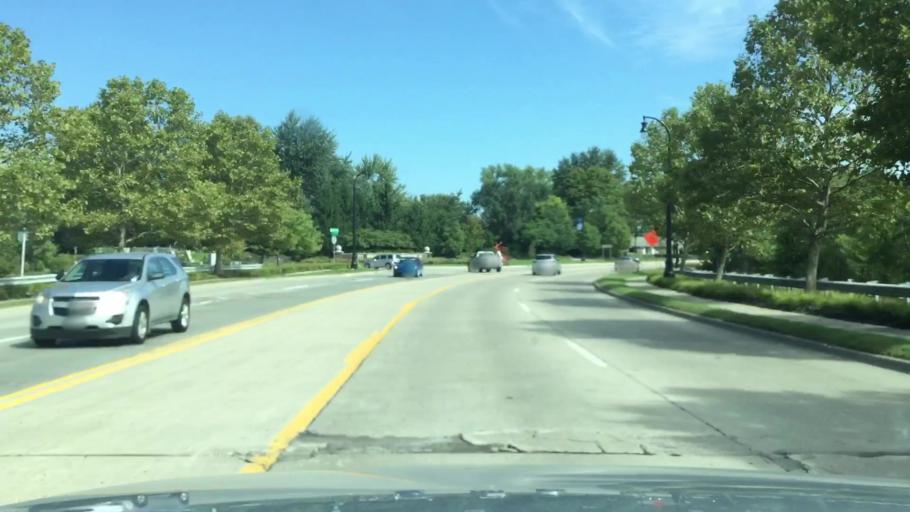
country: US
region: Michigan
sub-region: Wayne County
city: Belleville
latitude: 42.2128
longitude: -83.4922
